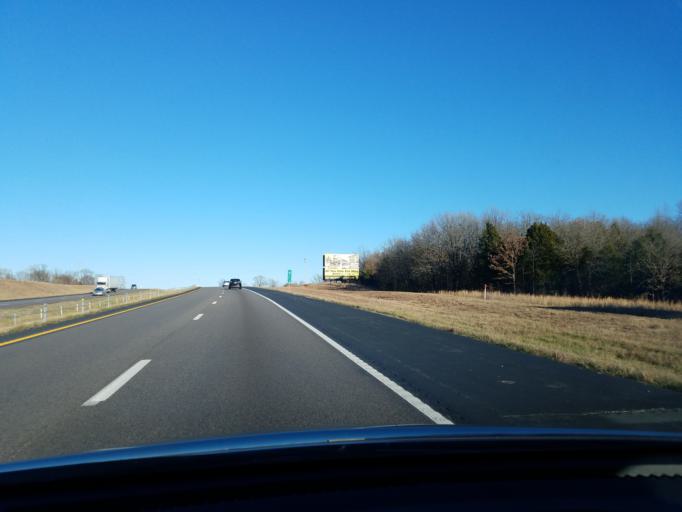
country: US
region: Missouri
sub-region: Phelps County
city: Saint James
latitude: 38.0151
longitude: -91.5849
